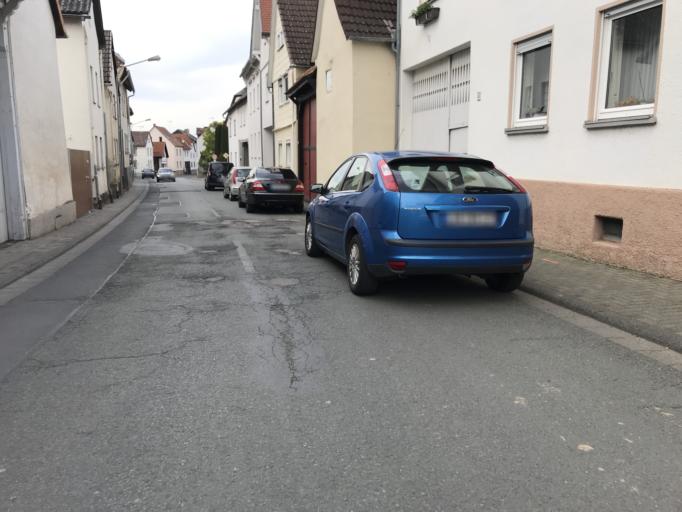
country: DE
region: Hesse
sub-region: Regierungsbezirk Giessen
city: Hoernsheim
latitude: 50.5106
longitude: 8.6172
